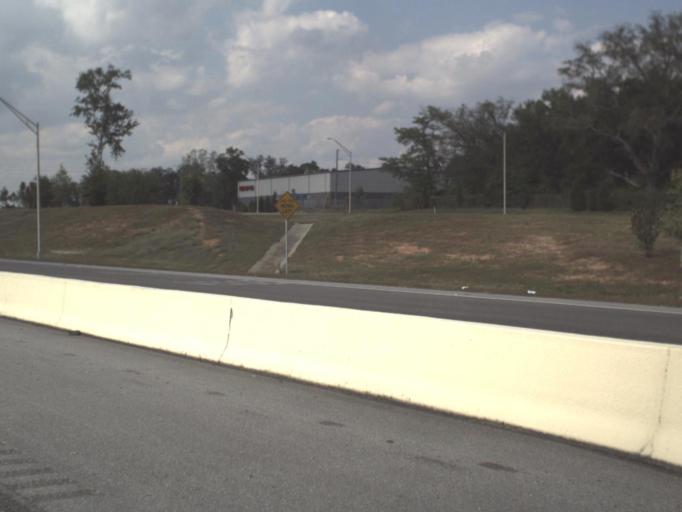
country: US
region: Florida
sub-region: Escambia County
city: Brent
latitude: 30.4792
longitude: -87.2301
